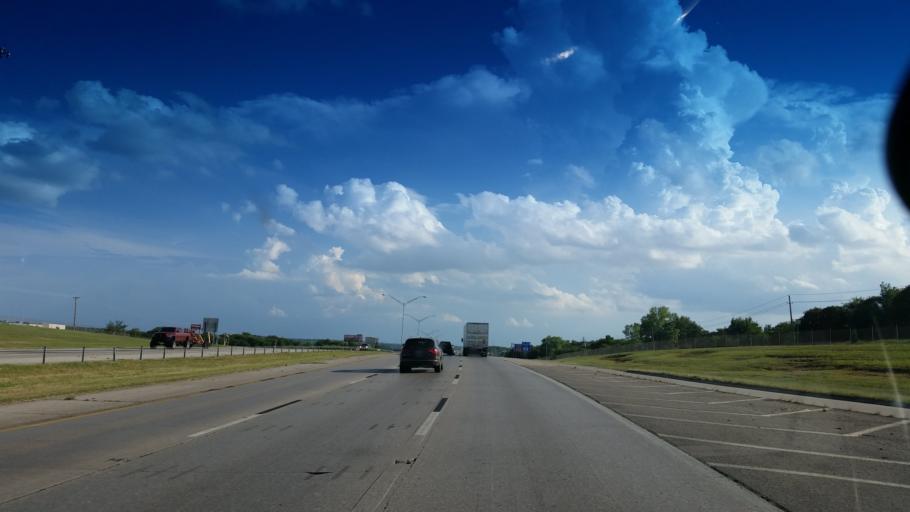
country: US
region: Oklahoma
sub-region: Oklahoma County
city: Spencer
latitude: 35.5634
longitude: -97.4529
